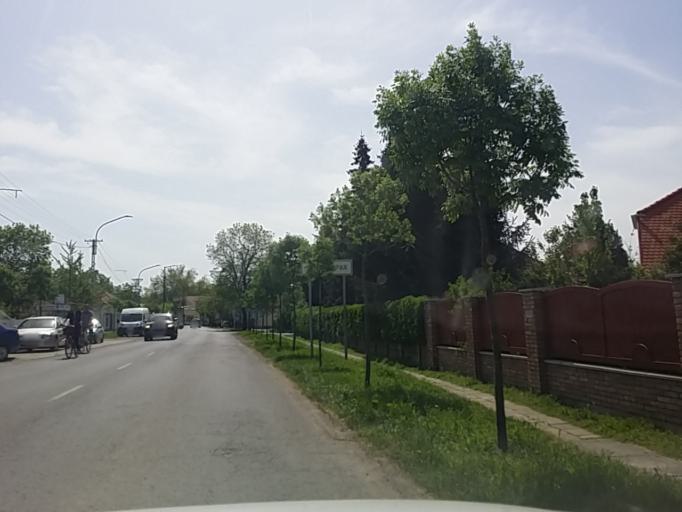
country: HU
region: Bekes
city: Gyula
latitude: 46.6485
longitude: 21.2840
